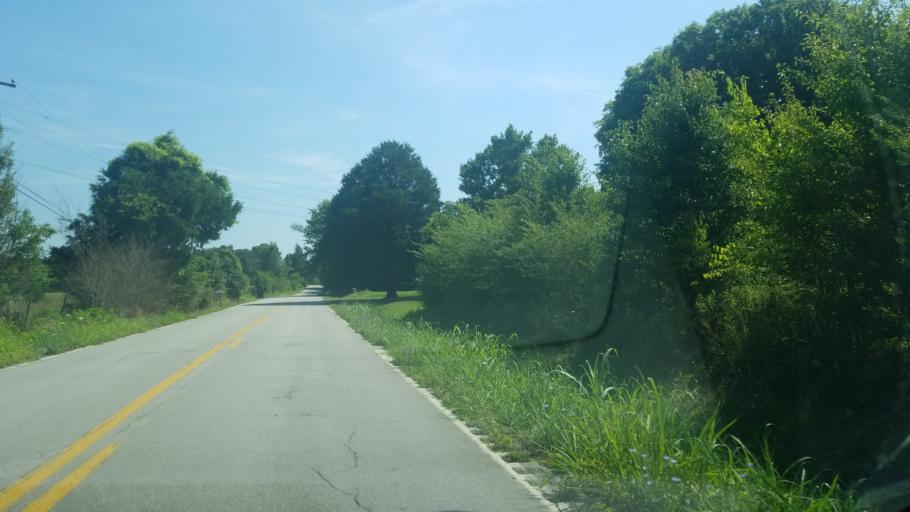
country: US
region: Tennessee
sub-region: Hamilton County
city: Sale Creek
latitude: 35.3246
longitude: -85.0185
